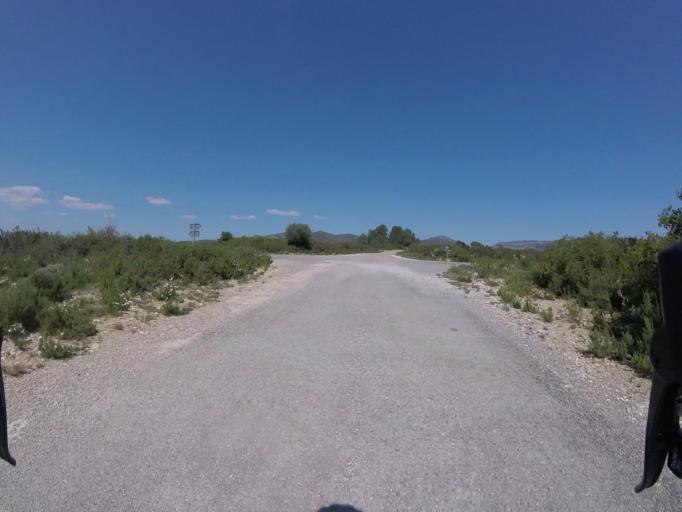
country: ES
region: Valencia
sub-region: Provincia de Castello
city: Sierra-Engarceran
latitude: 40.2244
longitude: -0.0217
